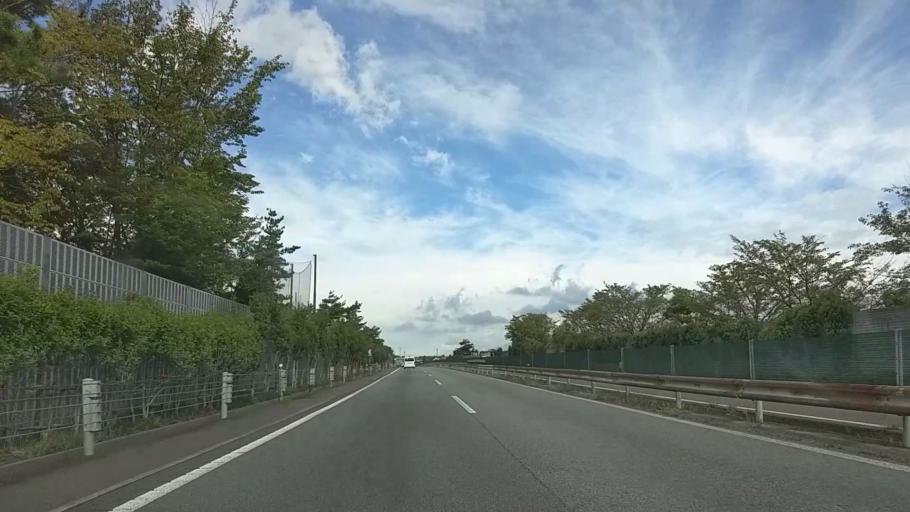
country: JP
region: Yamanashi
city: Ryuo
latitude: 35.6661
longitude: 138.5279
